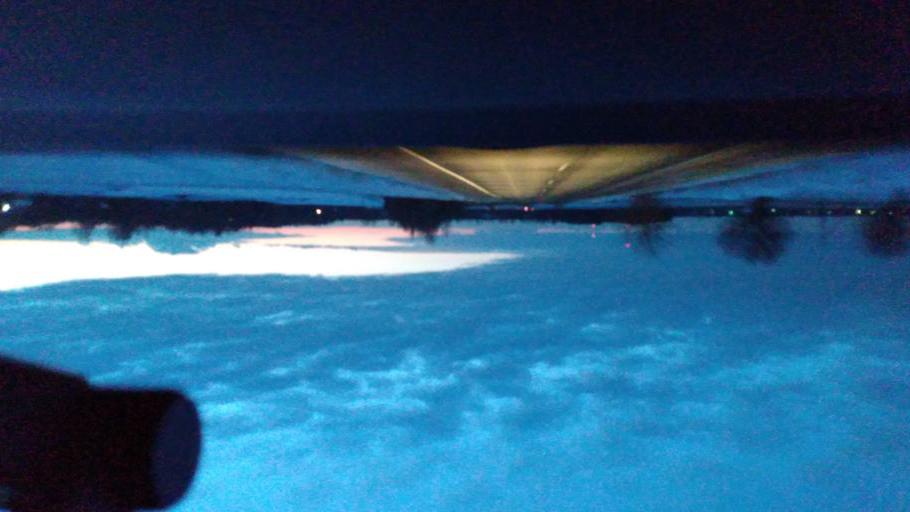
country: RU
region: Moskovskaya
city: Krasnaya Poyma
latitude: 55.1469
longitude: 39.2168
